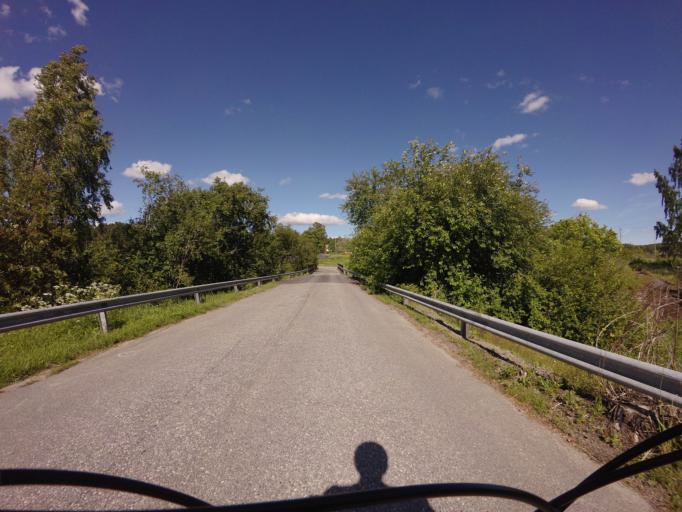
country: FI
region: Varsinais-Suomi
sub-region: Turku
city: Vahto
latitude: 60.5368
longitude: 22.3439
